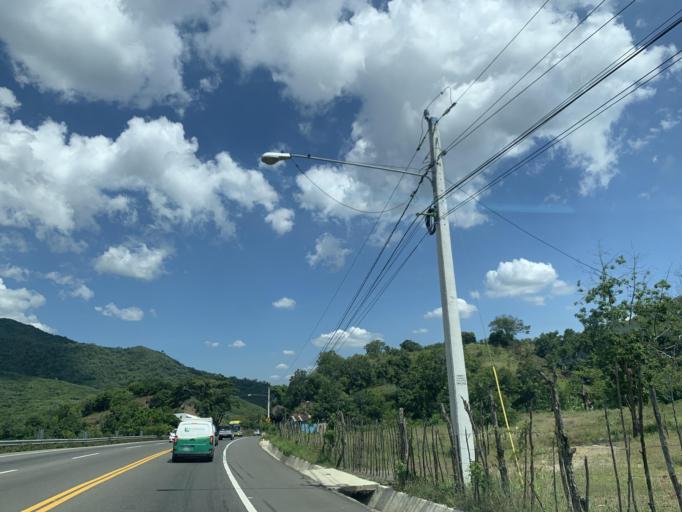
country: DO
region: Puerto Plata
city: Altamira
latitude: 19.6182
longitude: -70.8429
